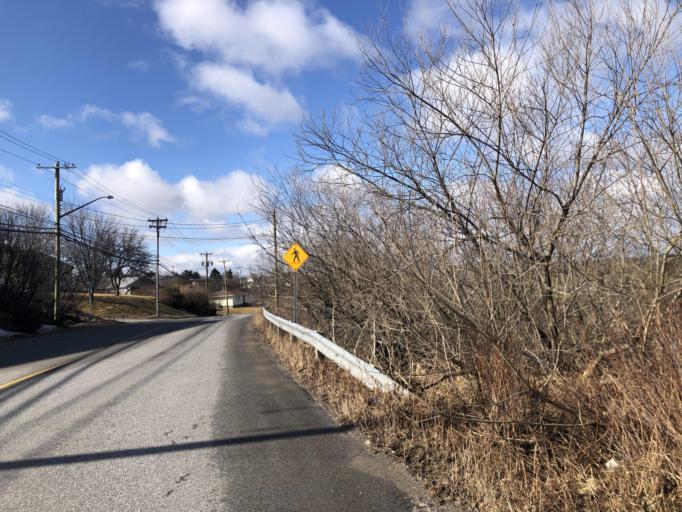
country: CA
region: New Brunswick
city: Saint John
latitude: 45.3206
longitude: -66.0029
